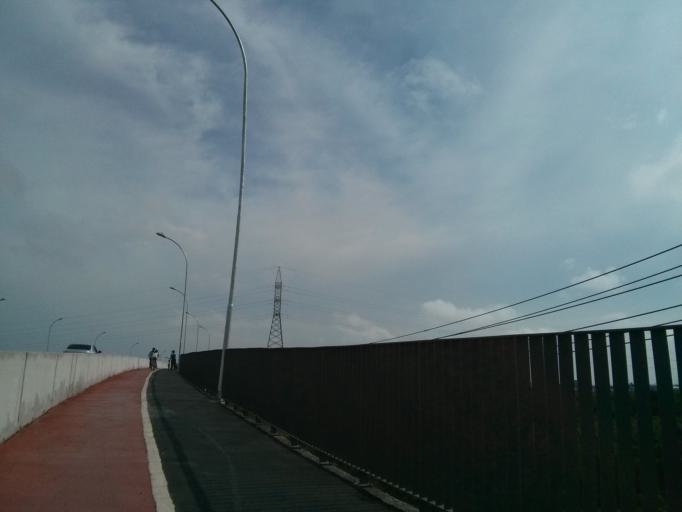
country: BR
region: Parana
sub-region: Sao Jose Dos Pinhais
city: Sao Jose dos Pinhais
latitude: -25.5254
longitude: -49.2249
